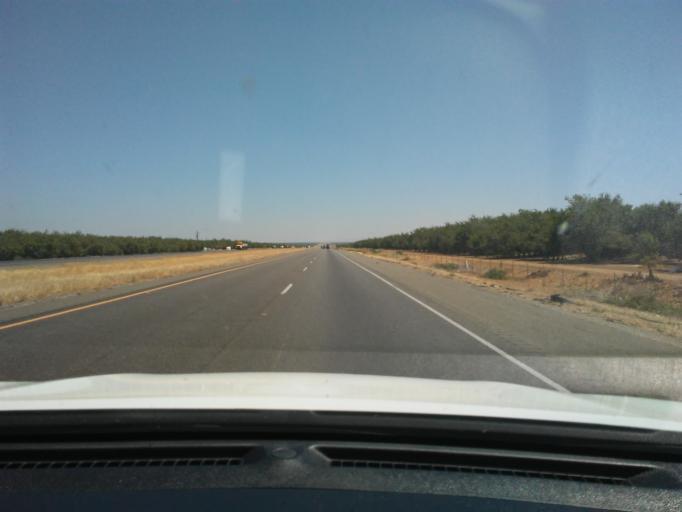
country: US
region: California
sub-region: Merced County
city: South Dos Palos
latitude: 36.8236
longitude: -120.7559
